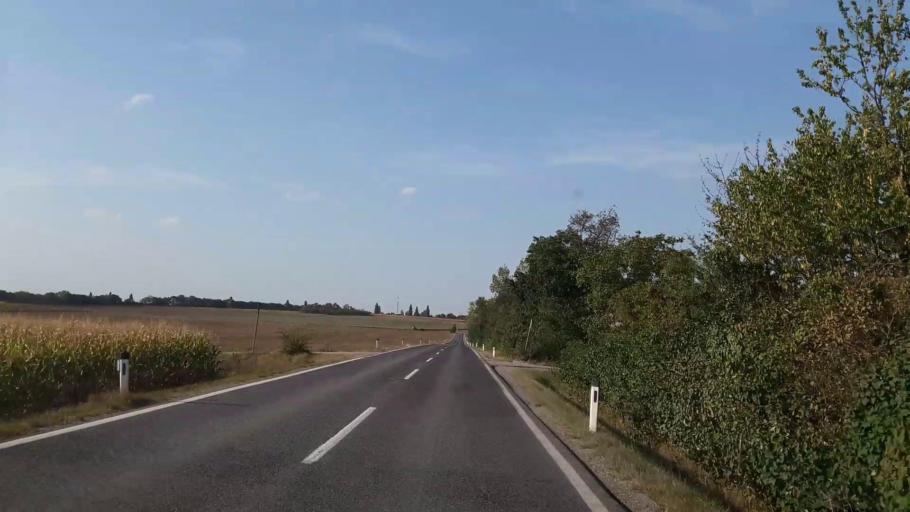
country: AT
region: Lower Austria
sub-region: Politischer Bezirk Ganserndorf
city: Mannsdorf an der Donau
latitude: 48.0994
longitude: 16.6687
